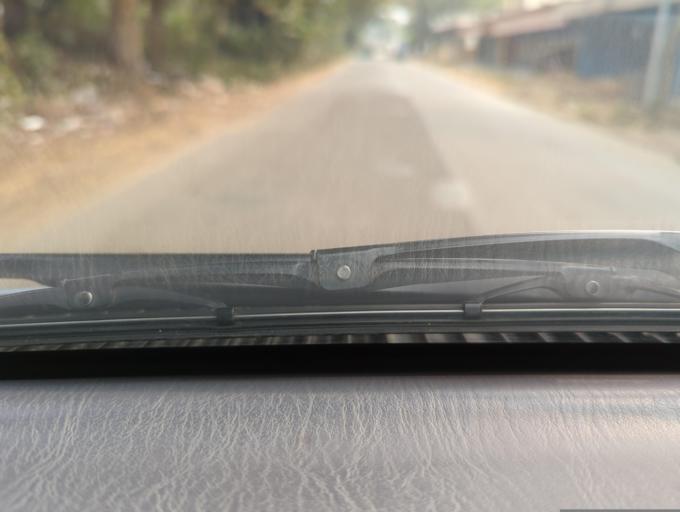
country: BD
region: Sylhet
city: Maulavi Bazar
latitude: 24.4962
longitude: 91.7452
